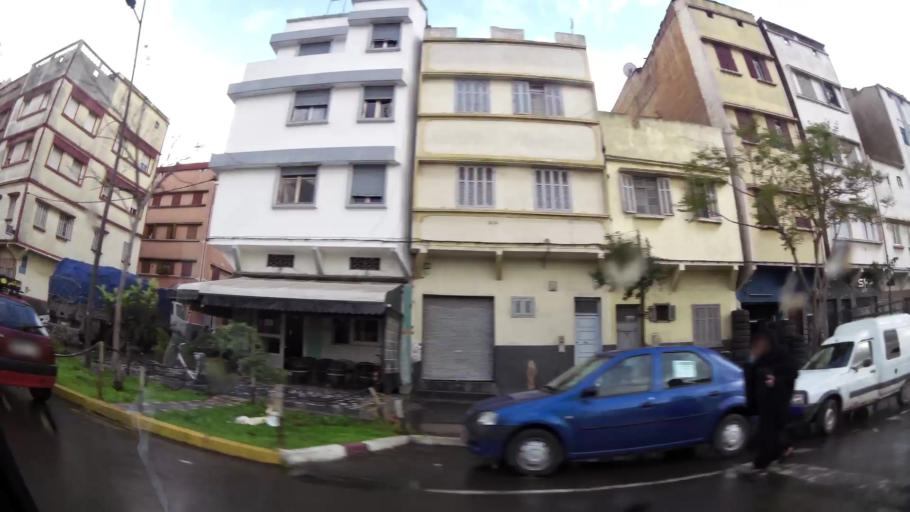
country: MA
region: Grand Casablanca
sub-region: Casablanca
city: Casablanca
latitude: 33.5568
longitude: -7.5893
